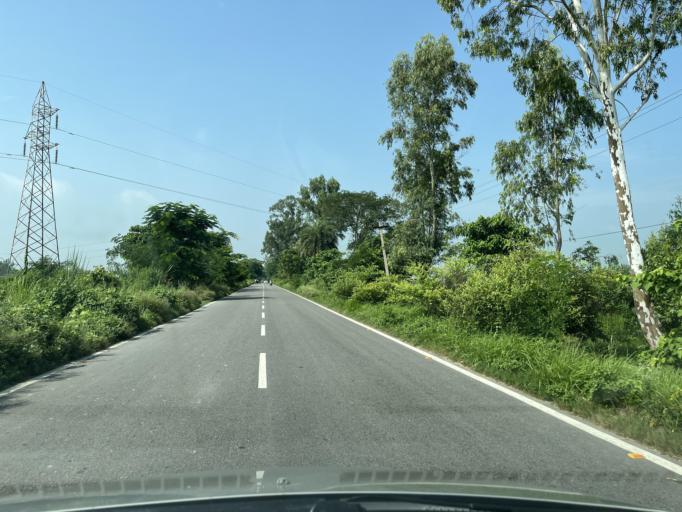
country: IN
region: Uttarakhand
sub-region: Udham Singh Nagar
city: Bazpur
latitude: 29.1963
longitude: 79.1981
